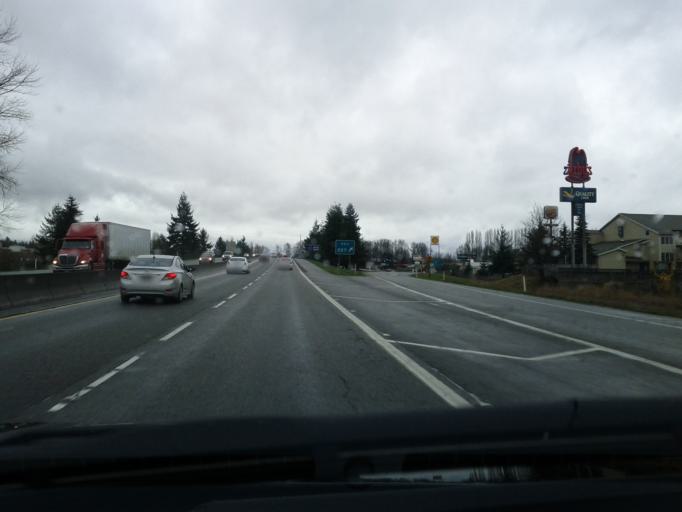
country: US
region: Washington
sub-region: Skagit County
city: Mount Vernon
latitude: 48.4390
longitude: -122.3411
